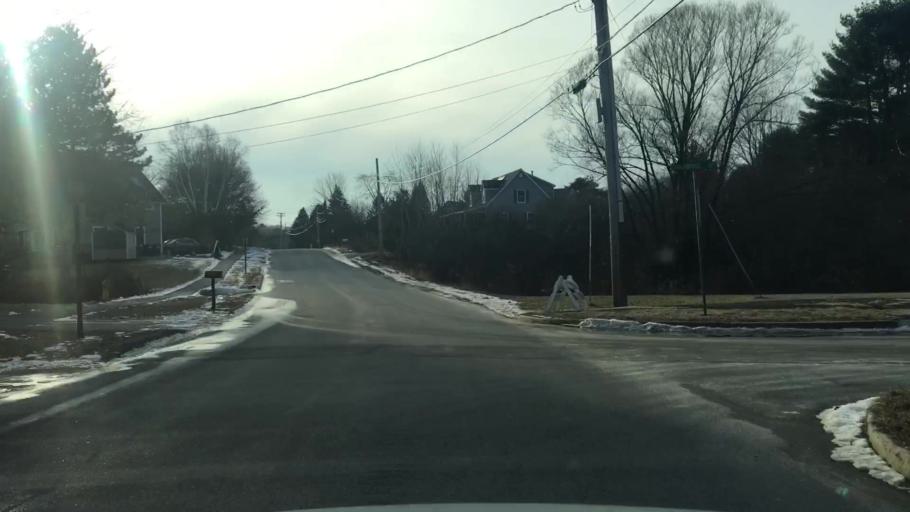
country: US
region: Maine
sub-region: Cumberland County
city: Yarmouth
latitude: 43.8096
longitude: -70.1877
